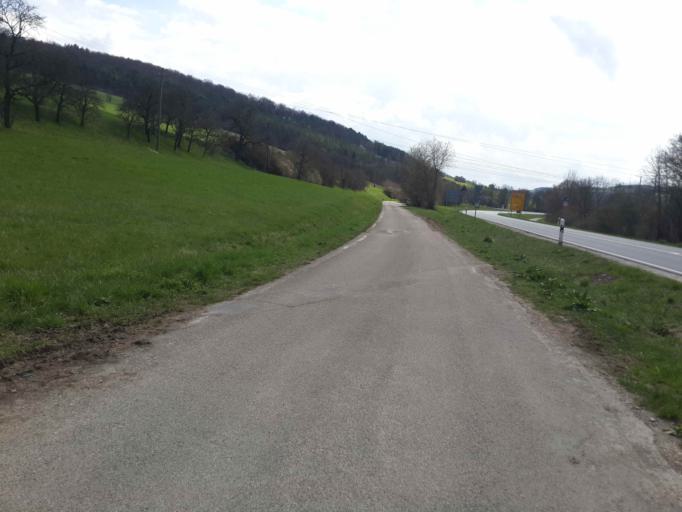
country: DE
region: Baden-Wuerttemberg
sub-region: Regierungsbezirk Stuttgart
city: Bad Mergentheim
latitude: 49.4754
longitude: 9.7729
